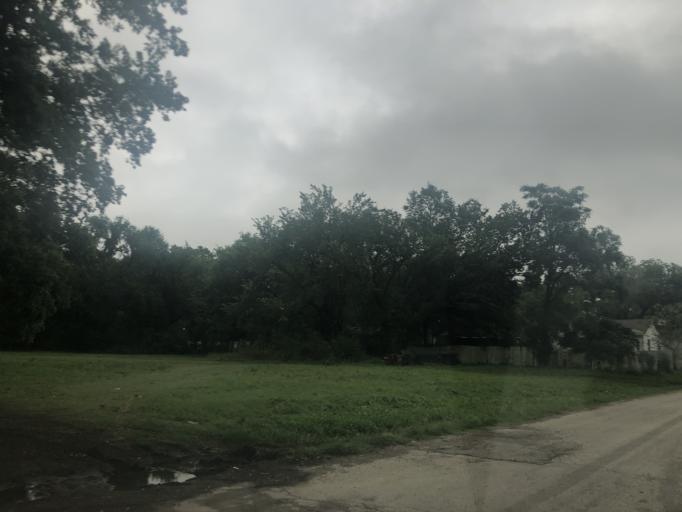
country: US
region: Texas
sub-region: Dallas County
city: Cockrell Hill
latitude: 32.7862
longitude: -96.8808
